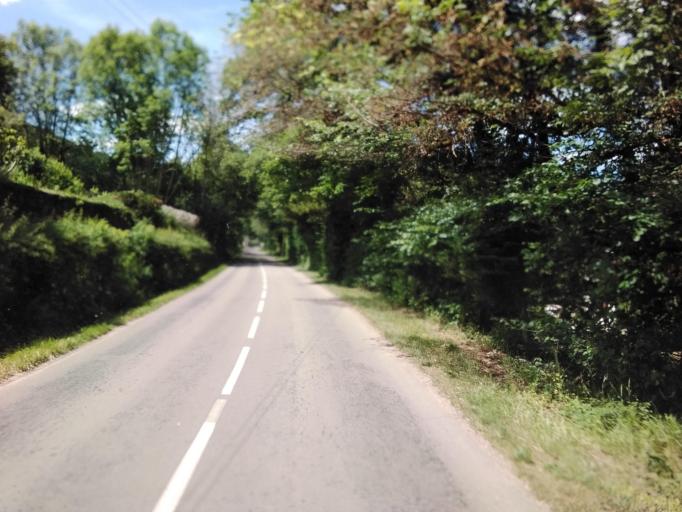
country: FR
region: Bourgogne
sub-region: Departement de l'Yonne
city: Avallon
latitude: 47.4769
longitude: 3.9154
